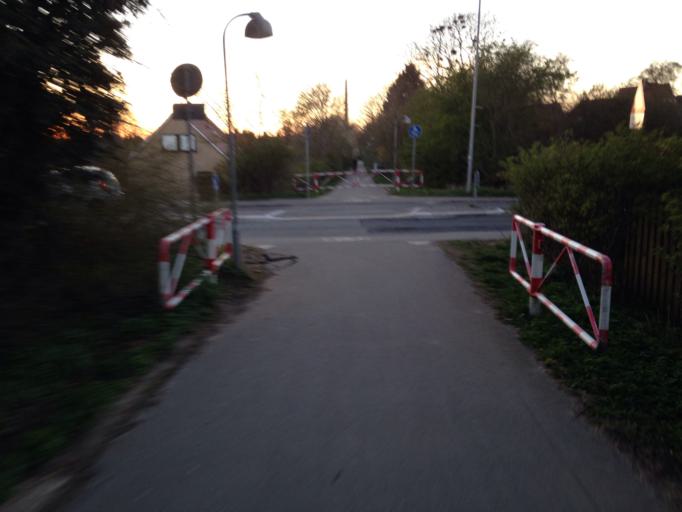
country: DK
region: Capital Region
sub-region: Hillerod Kommune
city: Hillerod
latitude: 55.9245
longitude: 12.3049
